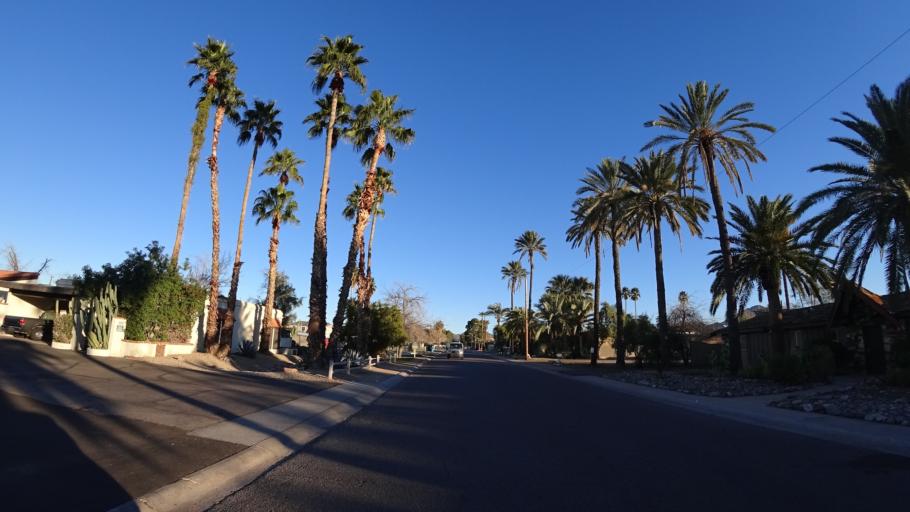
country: US
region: Arizona
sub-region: Maricopa County
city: Paradise Valley
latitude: 33.4820
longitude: -111.9999
